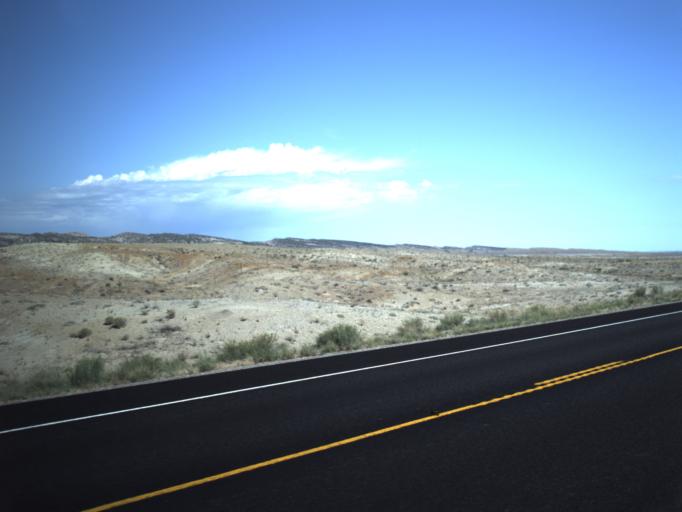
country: US
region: Utah
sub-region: Carbon County
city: East Carbon City
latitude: 39.1501
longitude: -110.3375
